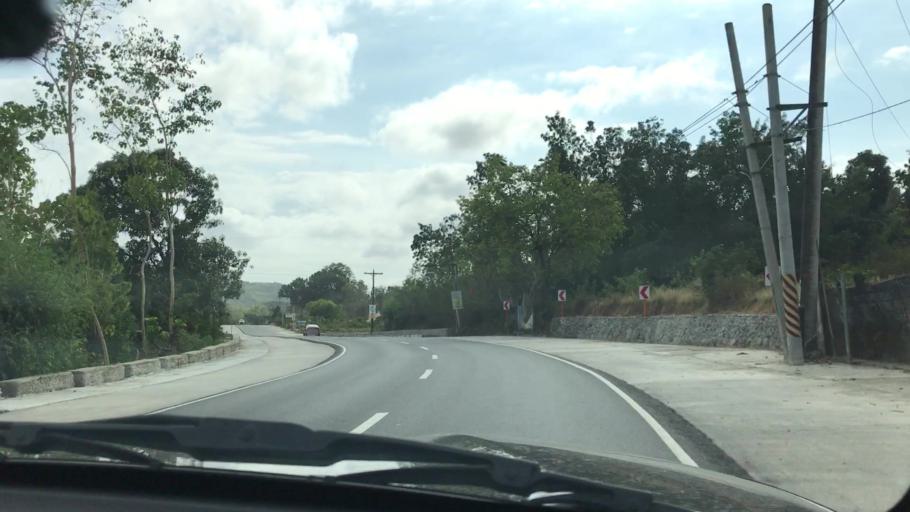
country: PH
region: Ilocos
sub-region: Province of La Union
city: Butubut Norte
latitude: 16.7814
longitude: 120.4157
